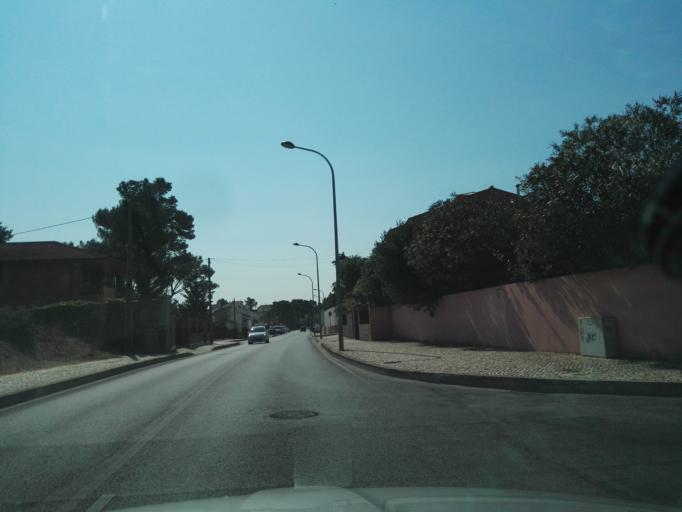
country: PT
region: Lisbon
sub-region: Cascais
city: Estoril
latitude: 38.7134
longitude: -9.3871
